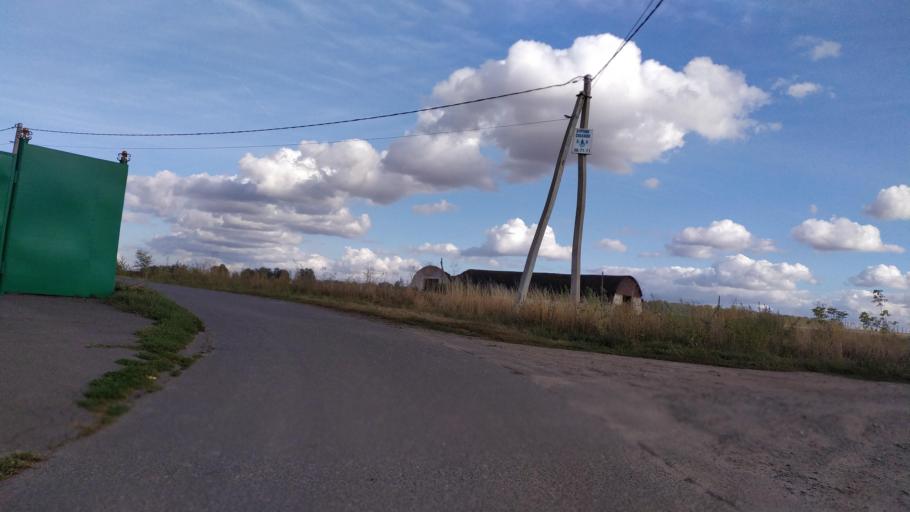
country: RU
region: Kursk
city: Kursk
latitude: 51.6276
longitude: 36.1548
